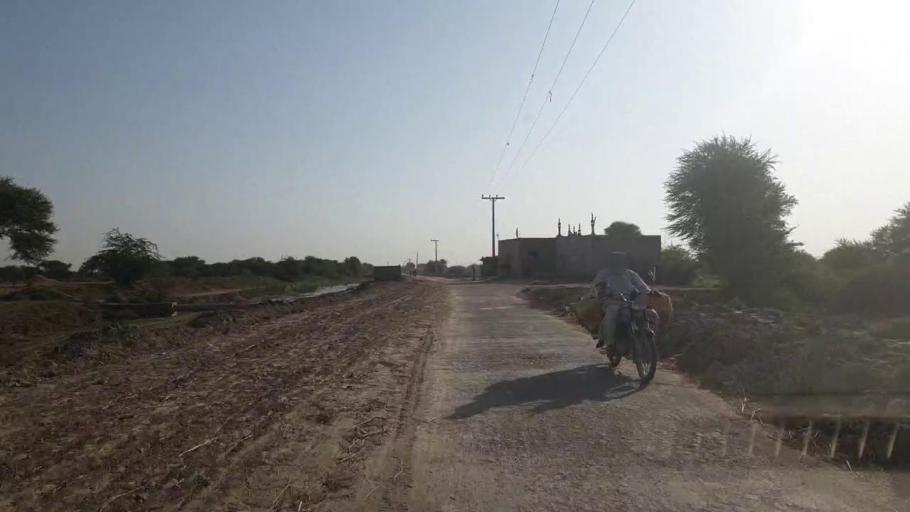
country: PK
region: Sindh
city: Talhar
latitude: 24.9204
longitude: 68.7459
